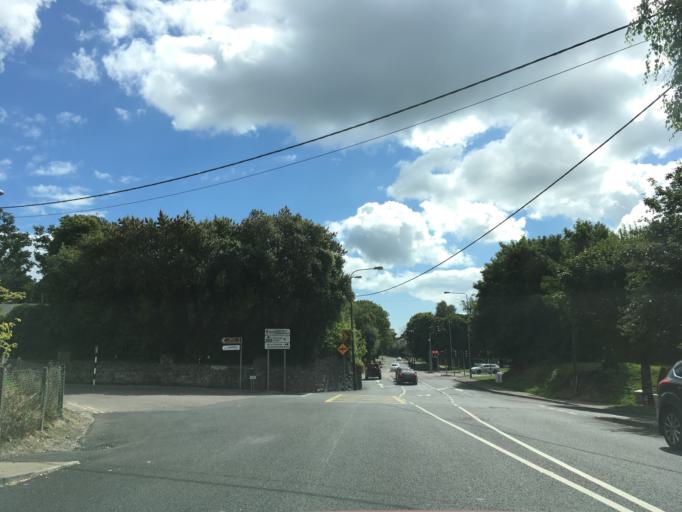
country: IE
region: Munster
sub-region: County Cork
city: Carrigaline
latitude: 51.8164
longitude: -8.3901
